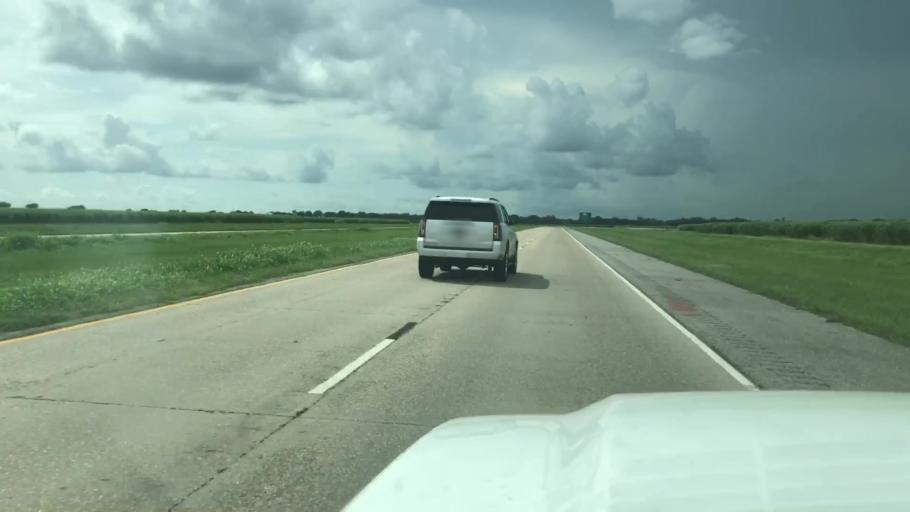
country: US
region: Louisiana
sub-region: Saint Mary Parish
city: Franklin
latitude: 29.7538
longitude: -91.4513
